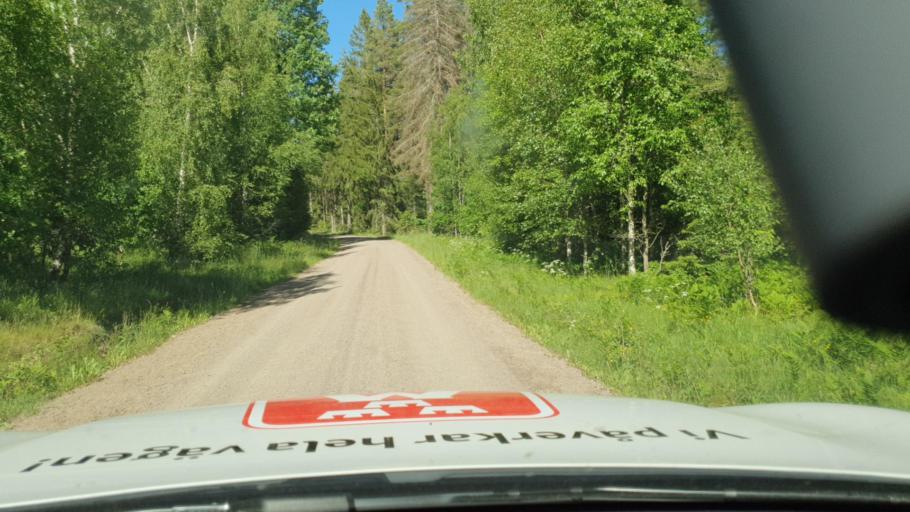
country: SE
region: Vaestra Goetaland
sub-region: Skovde Kommun
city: Skultorp
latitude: 58.3031
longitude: 13.8397
